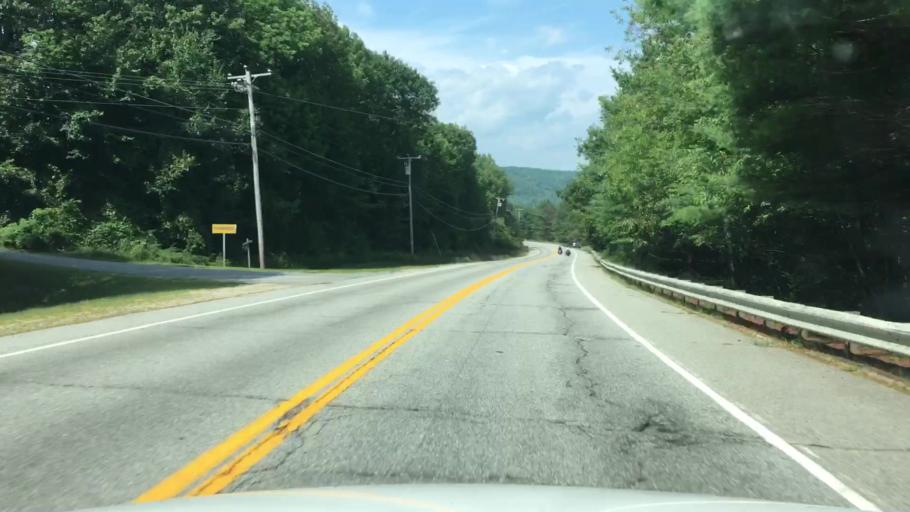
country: US
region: Maine
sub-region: Oxford County
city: Peru
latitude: 44.5016
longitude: -70.3998
